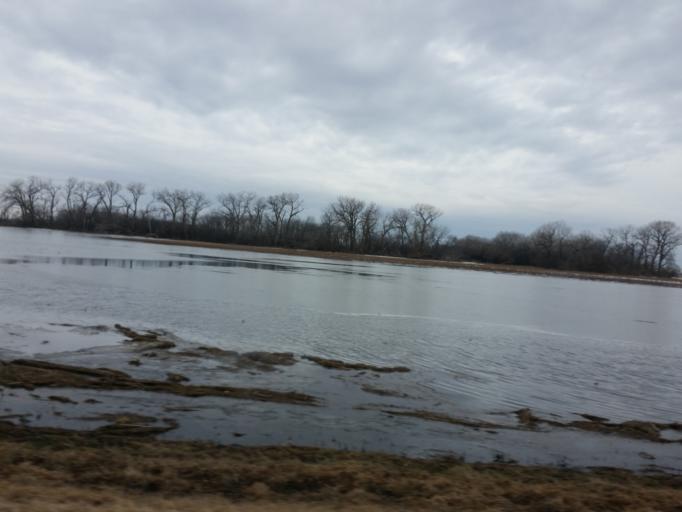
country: US
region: North Dakota
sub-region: Walsh County
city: Grafton
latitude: 48.4040
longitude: -97.4703
